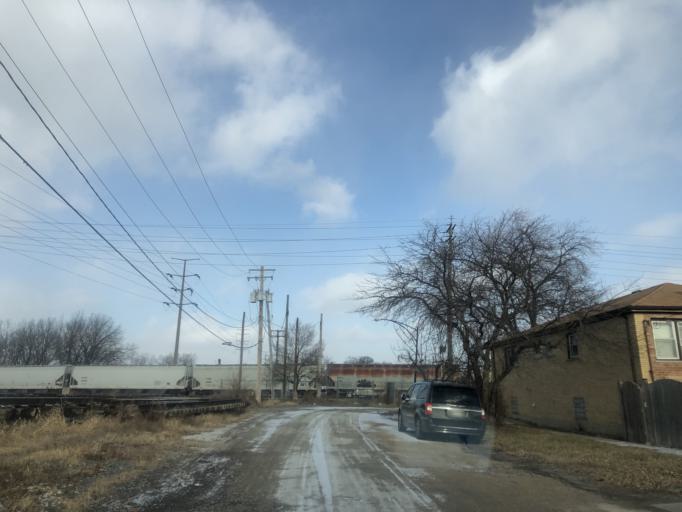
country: US
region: Illinois
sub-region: Cook County
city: Hometown
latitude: 41.7563
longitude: -87.7120
